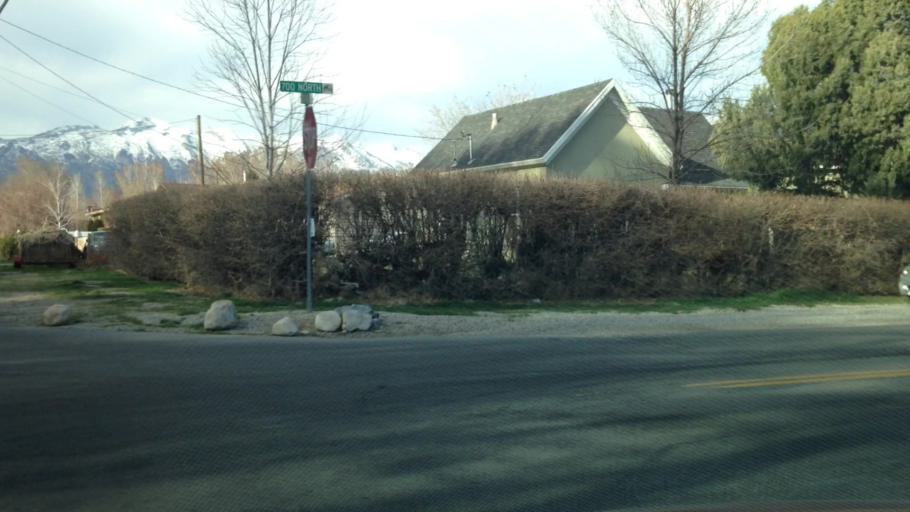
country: US
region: Utah
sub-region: Utah County
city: American Fork
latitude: 40.3910
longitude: -111.7931
